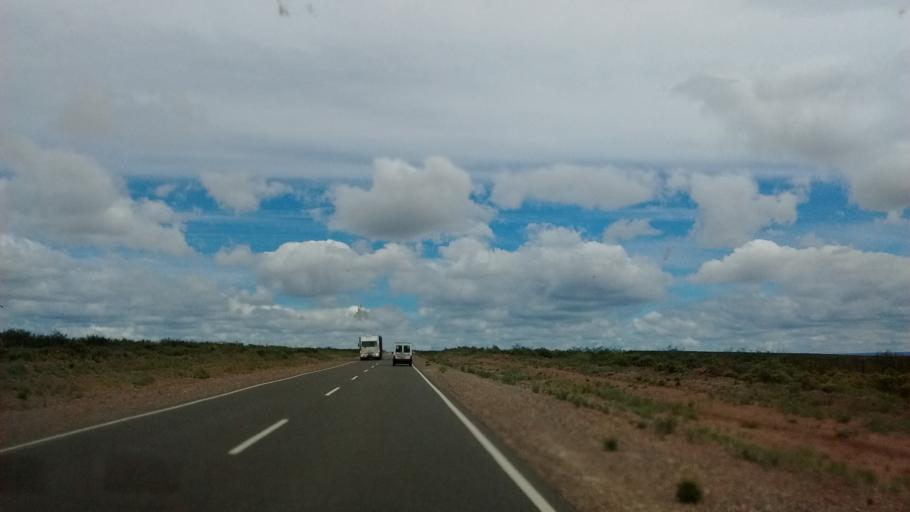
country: AR
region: Neuquen
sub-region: Departamento de Picun Leufu
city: Picun Leufu
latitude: -39.7520
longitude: -69.6295
